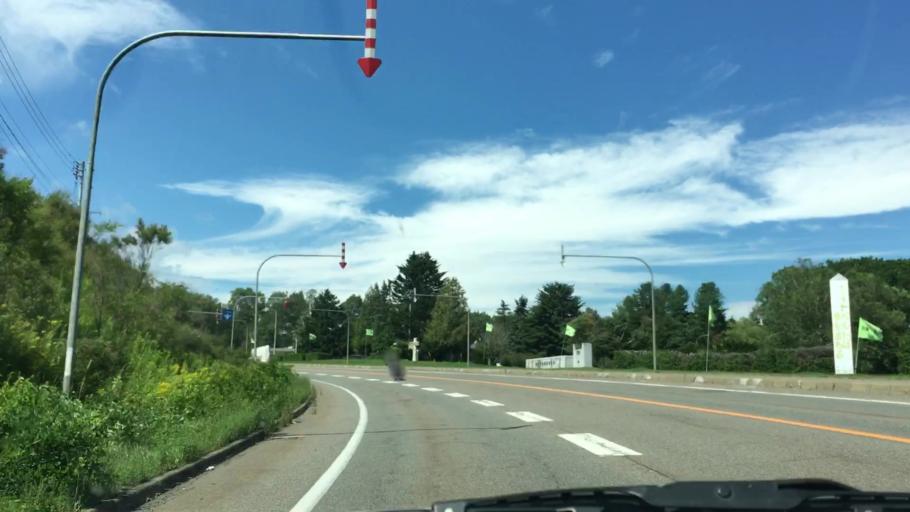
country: JP
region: Hokkaido
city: Otofuke
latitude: 43.2378
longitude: 143.5382
